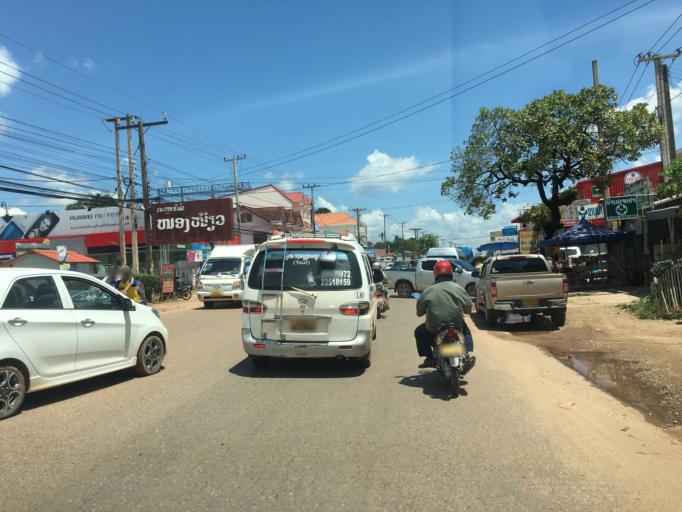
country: TH
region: Nong Khai
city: Si Chiang Mai
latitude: 18.0020
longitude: 102.5443
